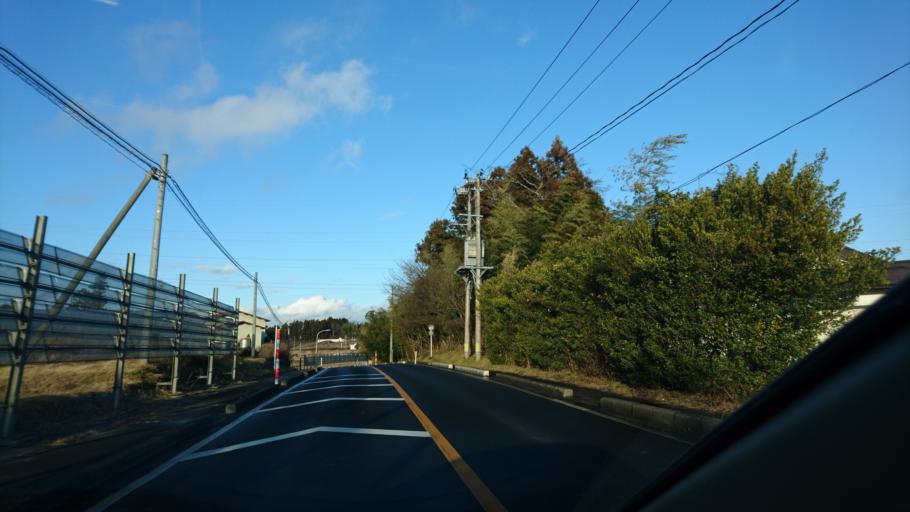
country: JP
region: Miyagi
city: Furukawa
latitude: 38.5993
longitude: 140.8659
